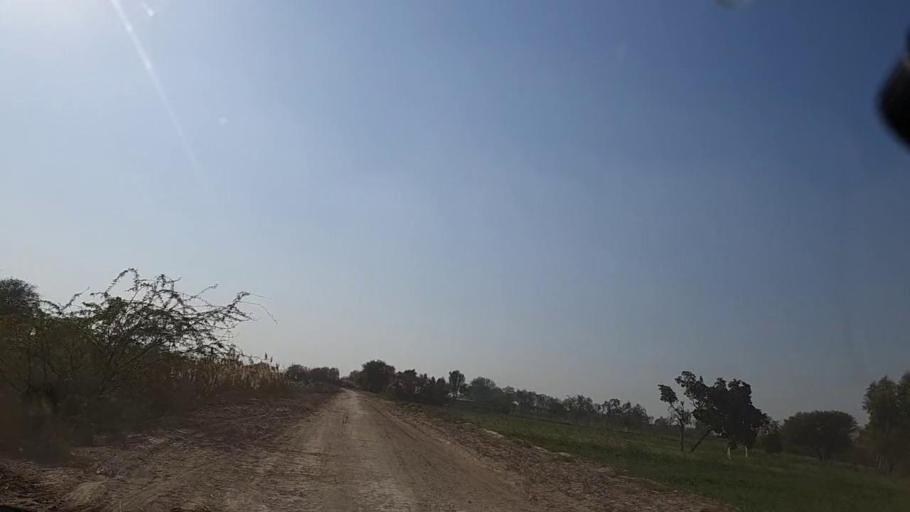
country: PK
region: Sindh
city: Mirpur Khas
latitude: 25.5208
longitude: 68.9233
